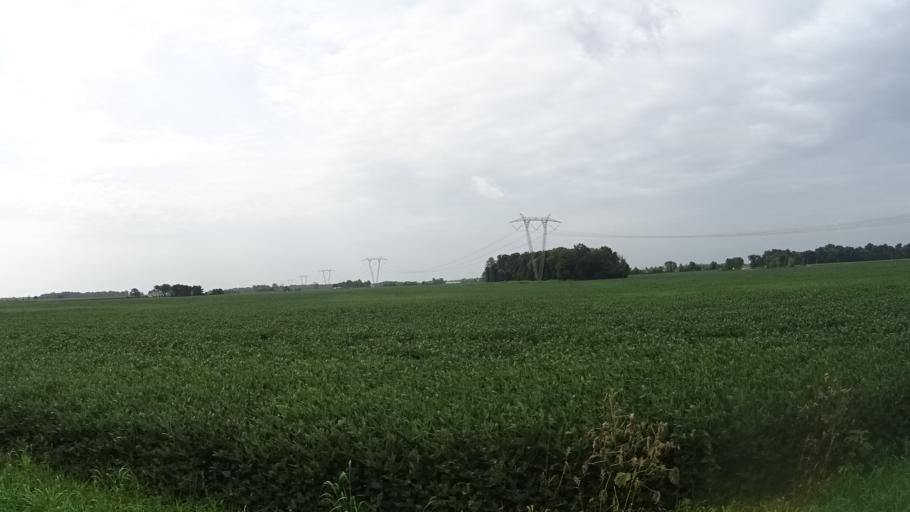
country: US
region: Indiana
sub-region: Madison County
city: Ingalls
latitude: 40.0025
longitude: -85.8198
